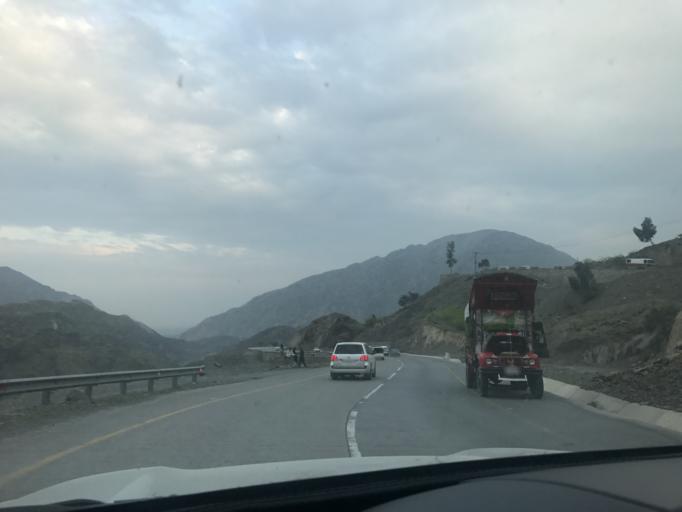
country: PK
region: Federally Administered Tribal Areas
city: Landi Kotal
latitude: 34.0103
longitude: 71.2957
